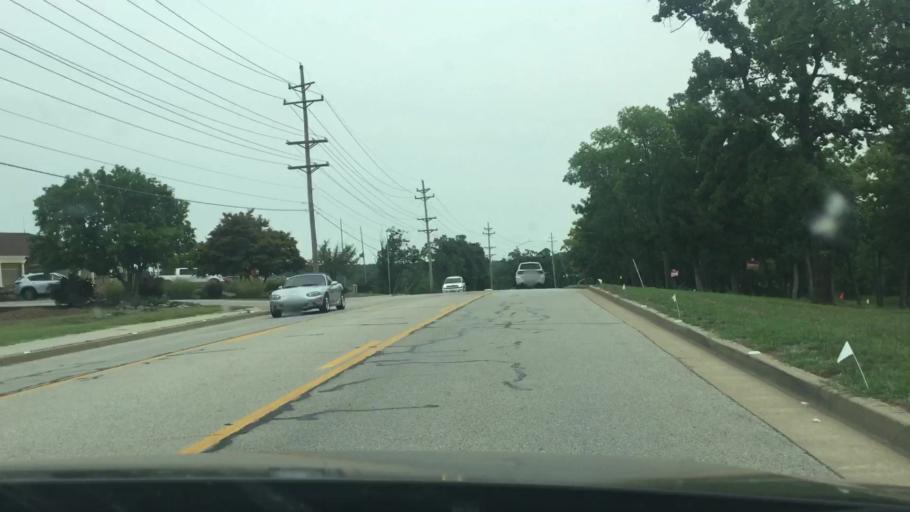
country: US
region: Missouri
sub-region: Camden County
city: Four Seasons
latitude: 38.1912
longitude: -92.6906
